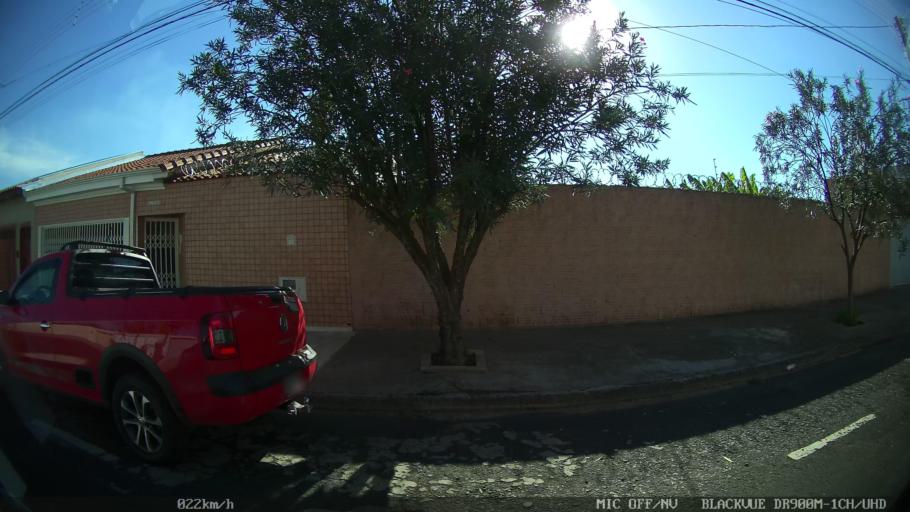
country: BR
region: Sao Paulo
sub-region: Franca
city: Franca
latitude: -20.5022
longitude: -47.4175
